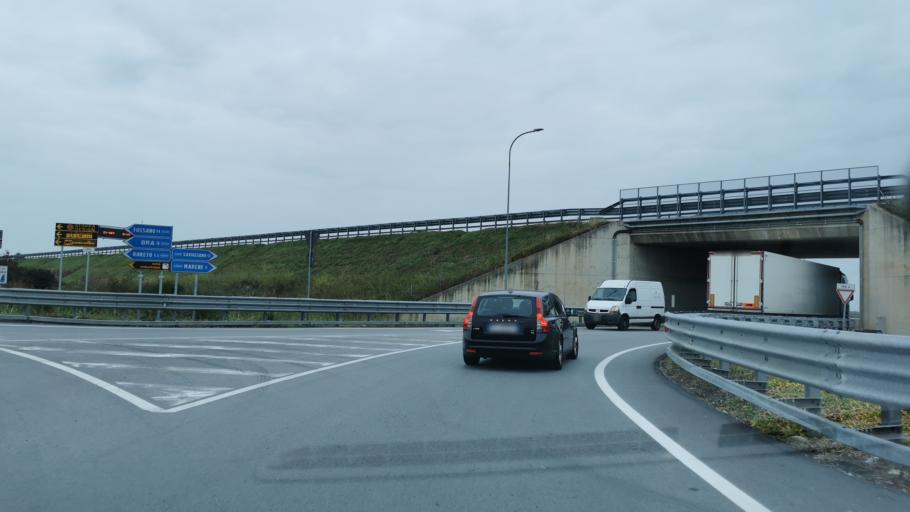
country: IT
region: Piedmont
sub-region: Provincia di Cuneo
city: Roreto
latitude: 44.6642
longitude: 7.8027
